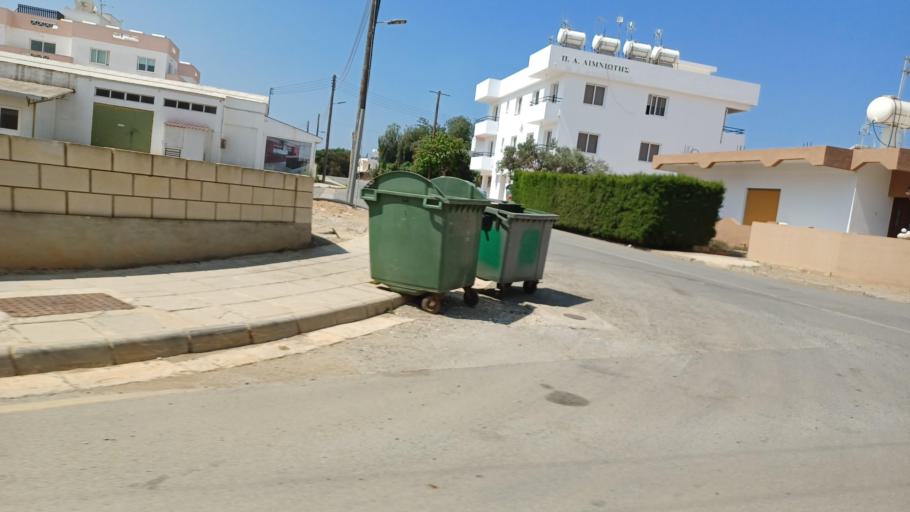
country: CY
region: Ammochostos
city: Liopetri
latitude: 34.9784
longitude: 33.8583
